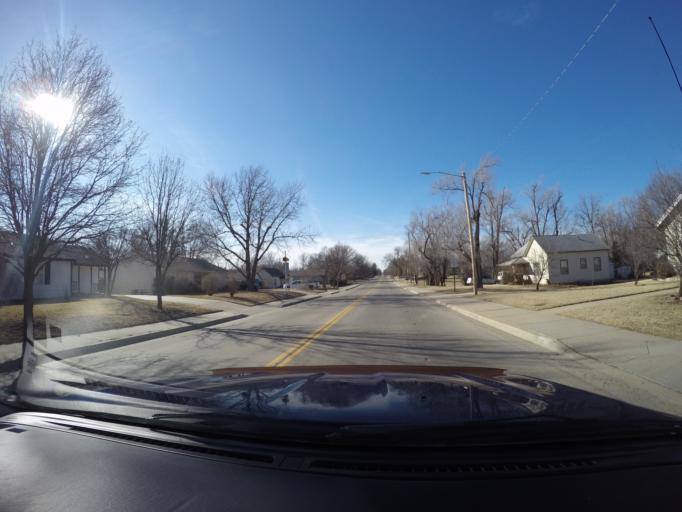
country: US
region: Kansas
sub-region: Harvey County
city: Newton
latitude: 38.0428
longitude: -97.3328
